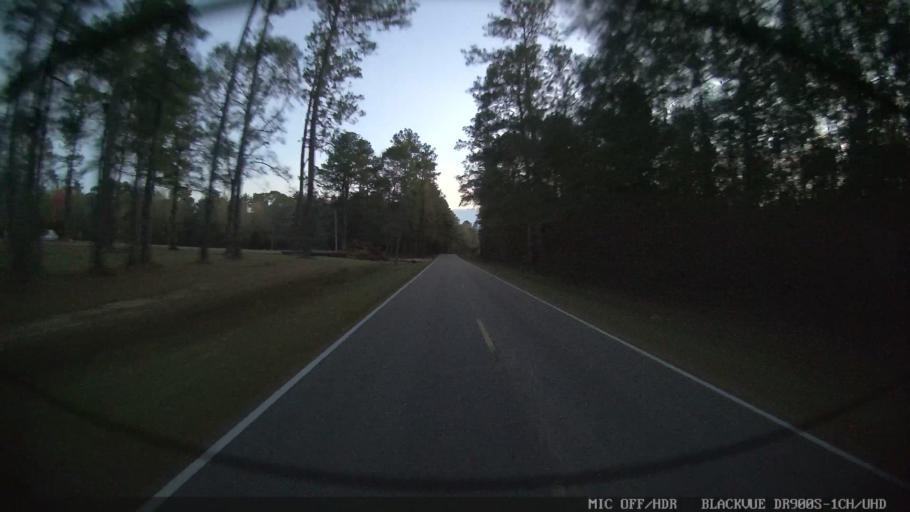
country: US
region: Mississippi
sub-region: Perry County
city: New Augusta
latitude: 31.1250
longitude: -89.1964
